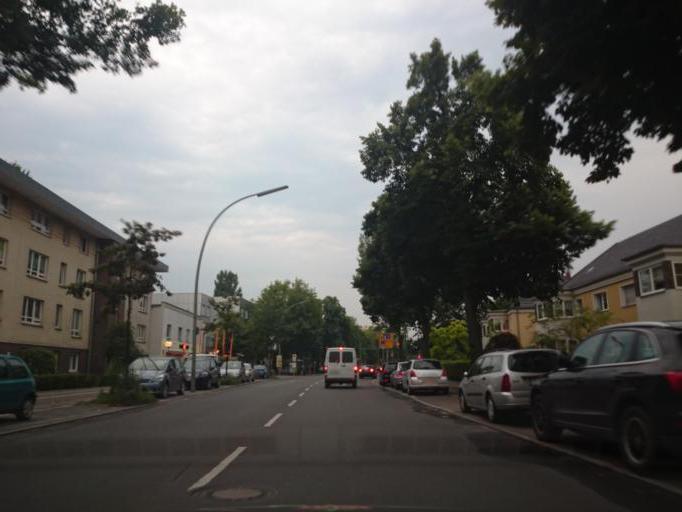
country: DE
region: Berlin
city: Lichterfelde
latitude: 52.4227
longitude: 13.2997
